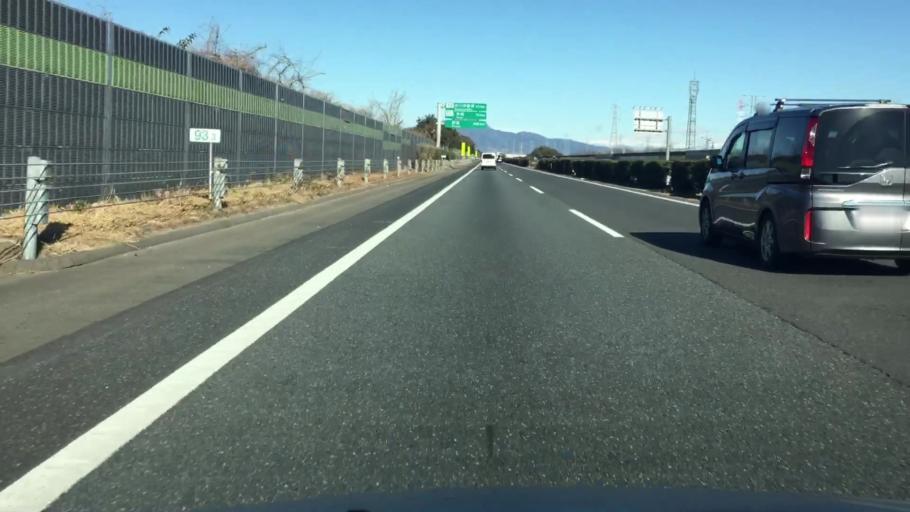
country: JP
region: Gunma
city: Maebashi-shi
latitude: 36.3850
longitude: 139.0264
